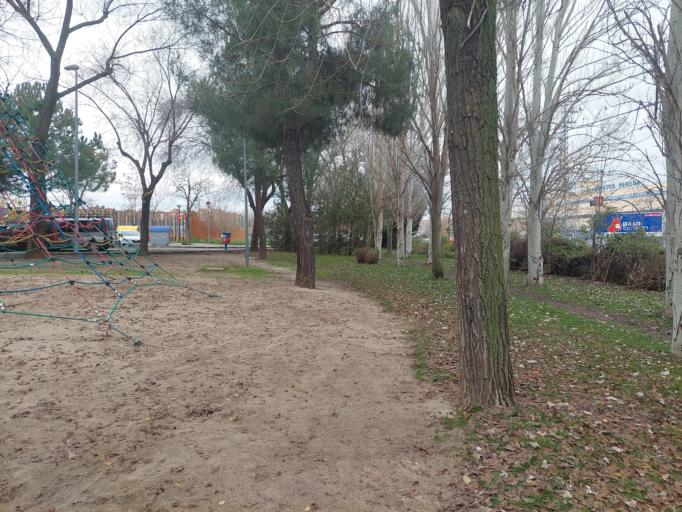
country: ES
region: Madrid
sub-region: Provincia de Madrid
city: Leganes
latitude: 40.3223
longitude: -3.7551
